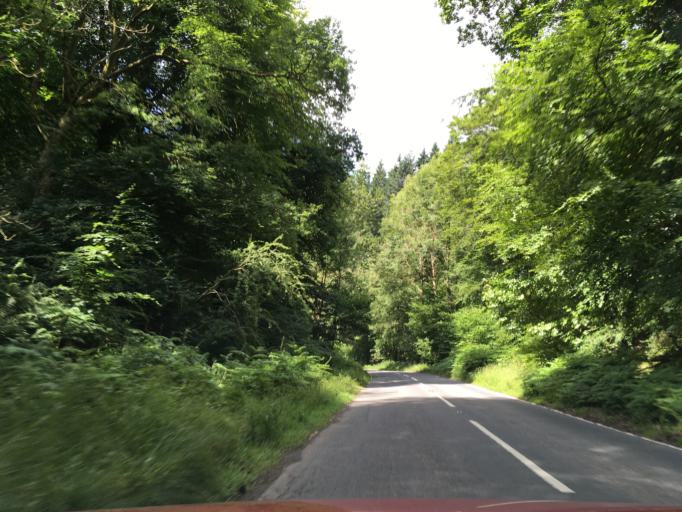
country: GB
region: England
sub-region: Gloucestershire
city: Cinderford
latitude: 51.7780
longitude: -2.5124
